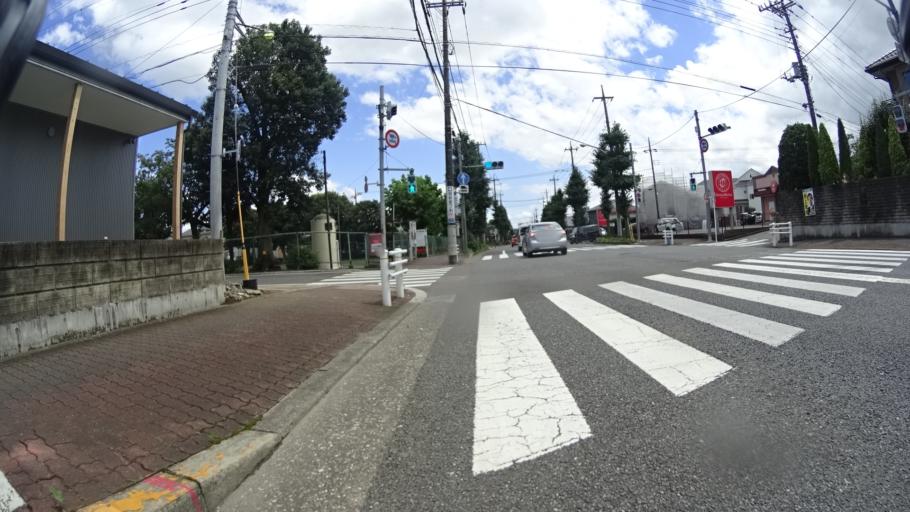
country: JP
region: Tokyo
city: Fussa
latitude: 35.7543
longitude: 139.3163
